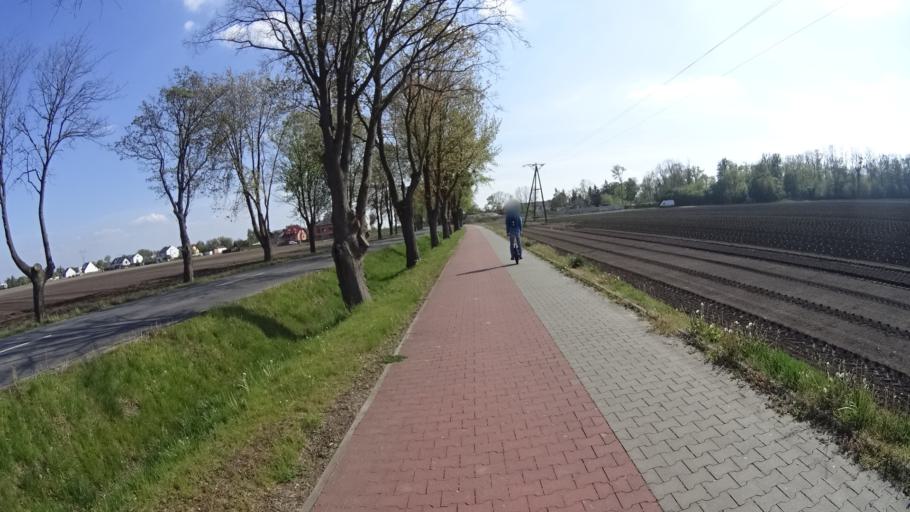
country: PL
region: Masovian Voivodeship
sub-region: Powiat warszawski zachodni
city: Stare Babice
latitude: 52.2356
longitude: 20.8163
